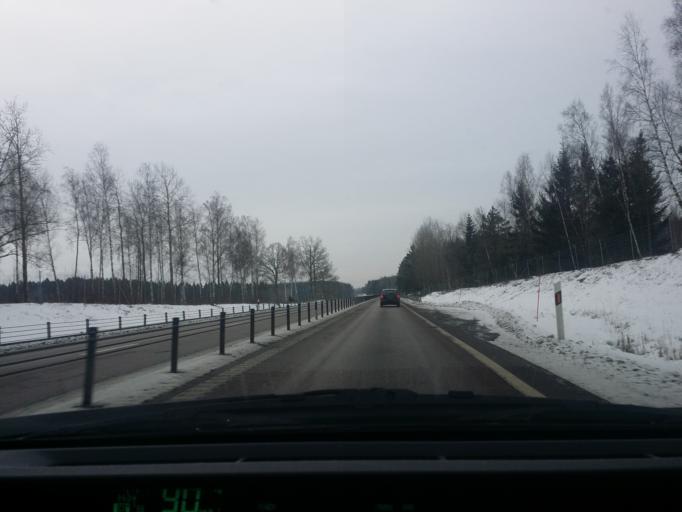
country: SE
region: Vaestra Goetaland
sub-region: Skovde Kommun
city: Stopen
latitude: 58.5431
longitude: 13.8115
